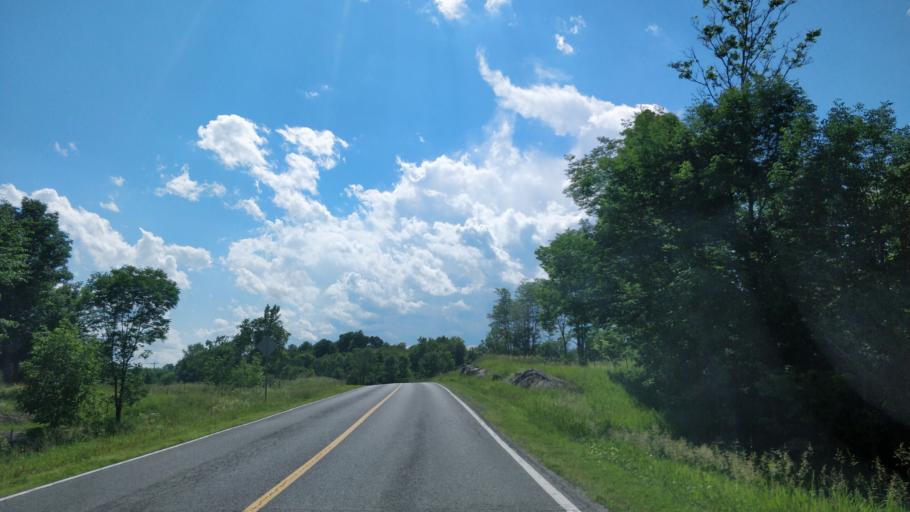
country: CA
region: Ontario
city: Perth
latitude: 44.7569
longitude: -76.4778
